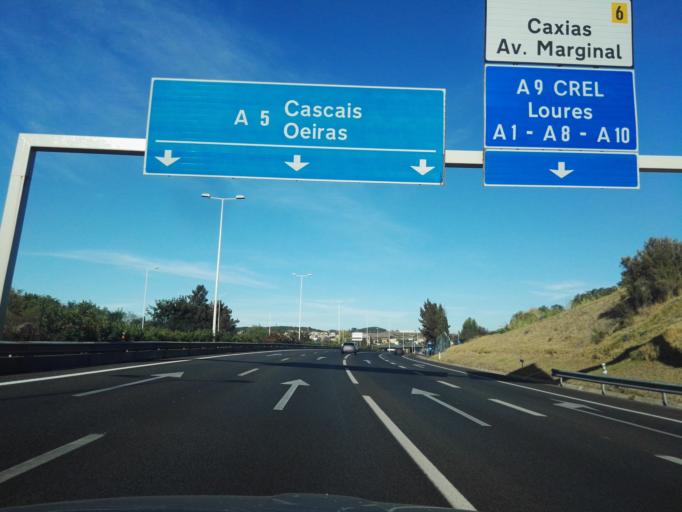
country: PT
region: Lisbon
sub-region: Oeiras
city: Quejas
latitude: 38.7139
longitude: -9.2636
